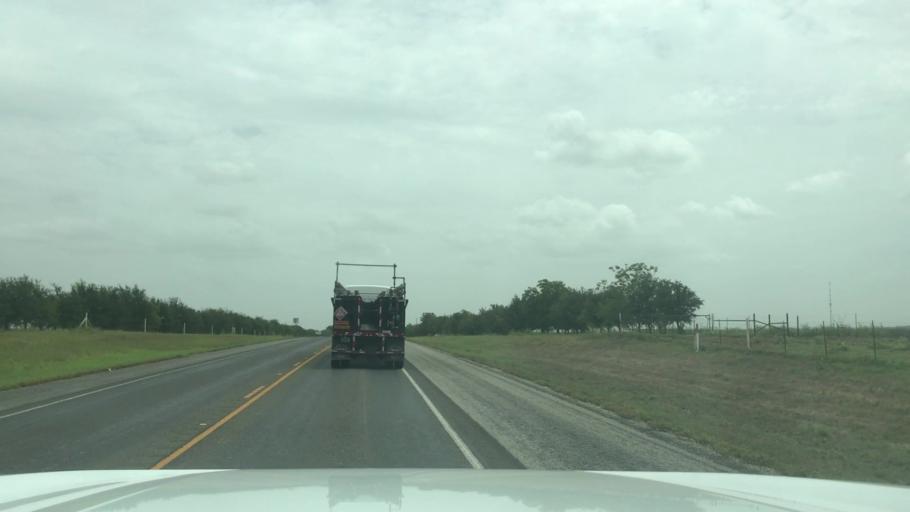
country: US
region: Texas
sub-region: Bosque County
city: Clifton
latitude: 31.8027
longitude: -97.6019
